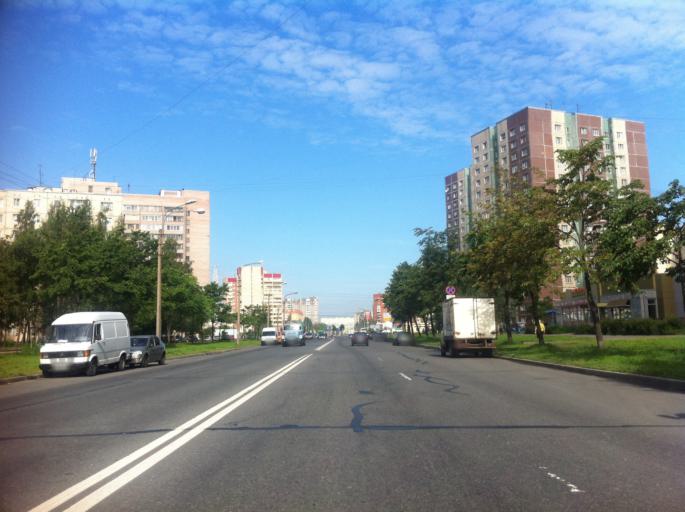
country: RU
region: St.-Petersburg
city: Uritsk
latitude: 59.8515
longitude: 30.2033
